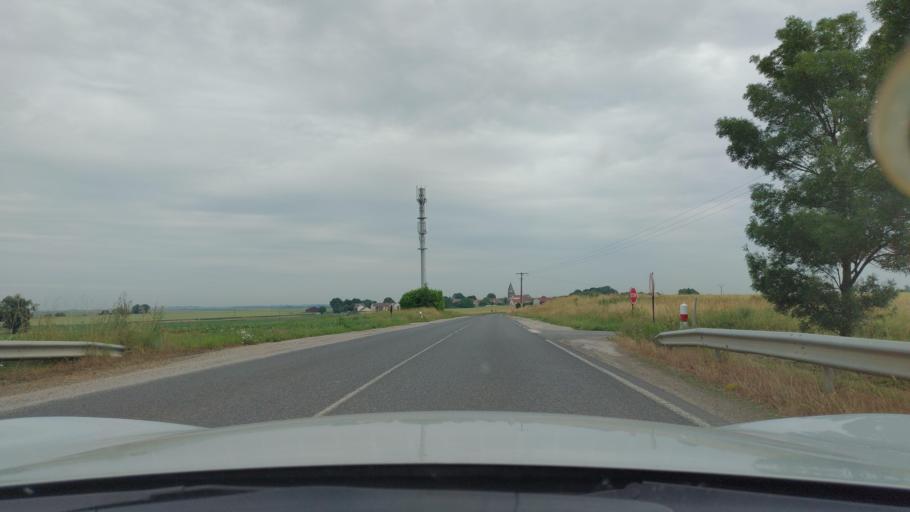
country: FR
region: Ile-de-France
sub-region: Departement de Seine-et-Marne
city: Cregy-les-Meaux
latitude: 49.0099
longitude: 2.8794
